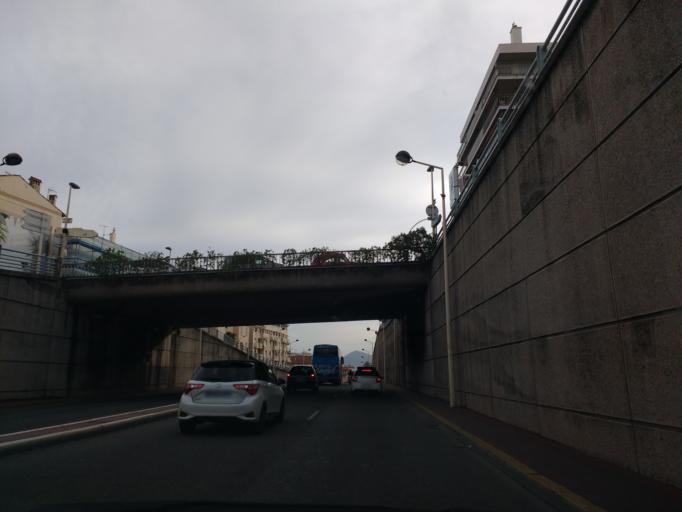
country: FR
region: Provence-Alpes-Cote d'Azur
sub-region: Departement des Alpes-Maritimes
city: Cannes
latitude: 43.5520
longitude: 7.0094
